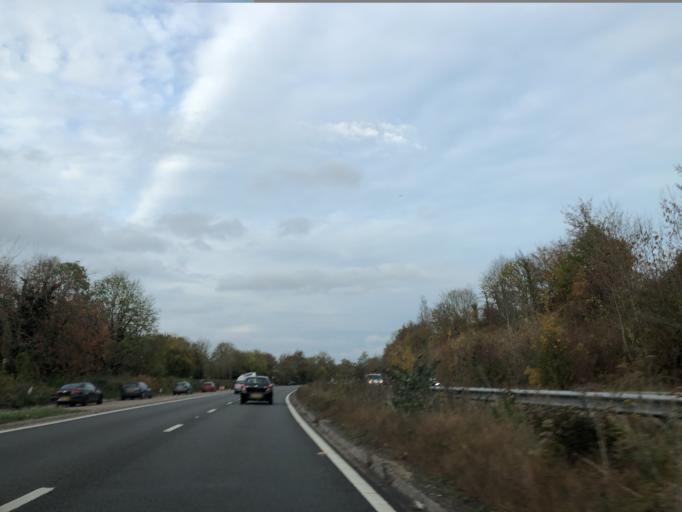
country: GB
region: England
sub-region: Royal Borough of Windsor and Maidenhead
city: Bisham
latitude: 51.5418
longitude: -0.7878
